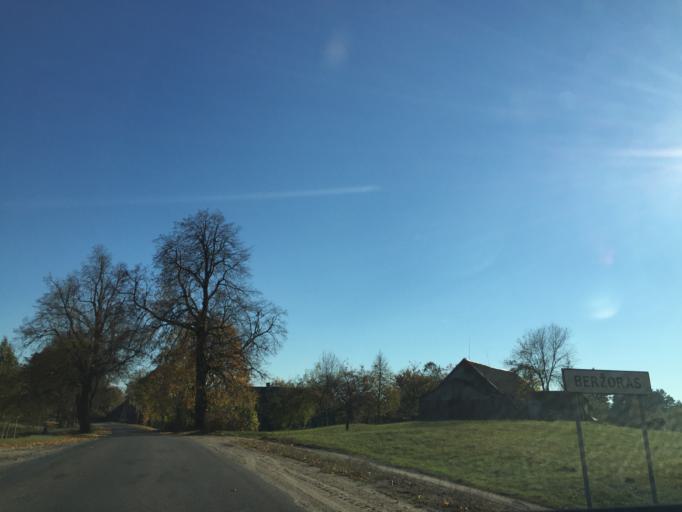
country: LT
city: Plateliai
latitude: 56.0281
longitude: 21.8082
